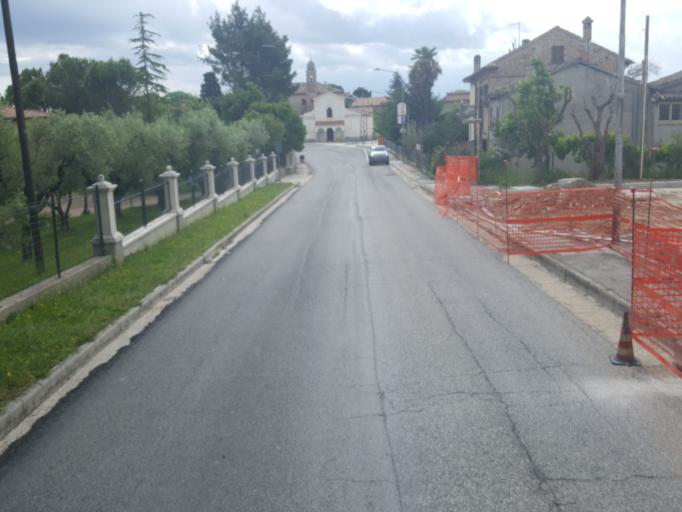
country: IT
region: The Marches
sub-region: Provincia di Macerata
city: Pollenza
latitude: 43.2597
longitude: 13.3563
